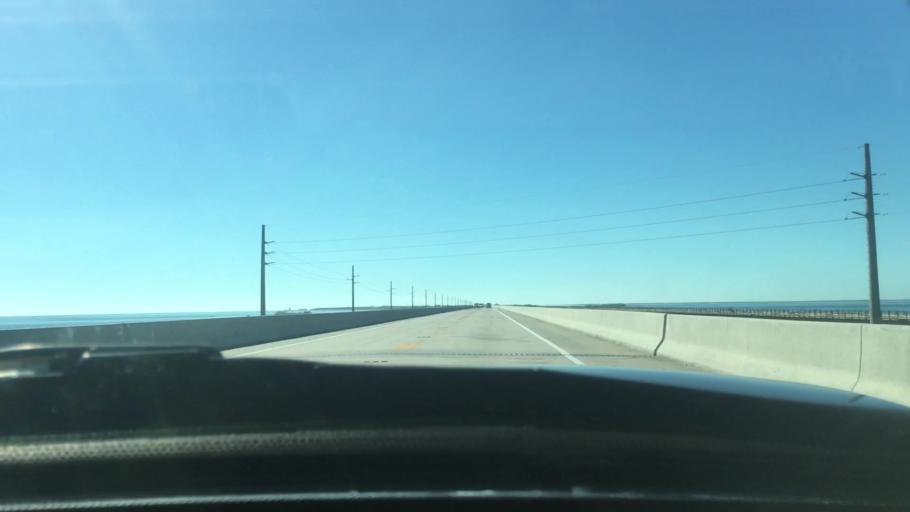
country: US
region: Florida
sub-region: Monroe County
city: Marathon
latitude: 24.6891
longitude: -81.2043
